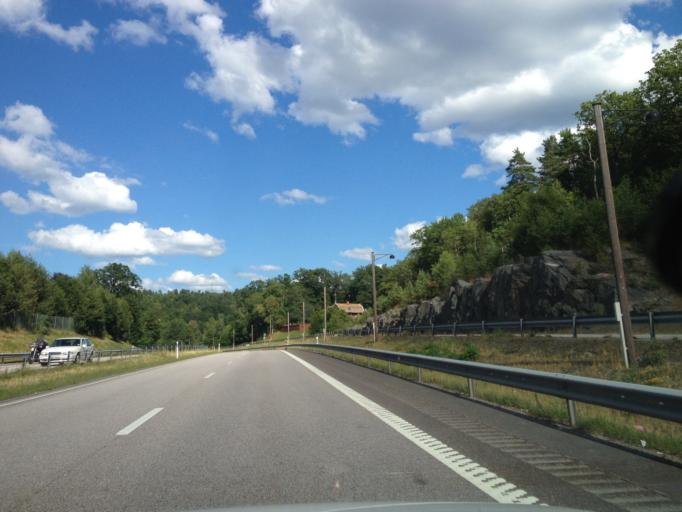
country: SE
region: Vaestra Goetaland
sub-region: Alingsas Kommun
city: Ingared
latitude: 57.8115
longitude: 12.4066
